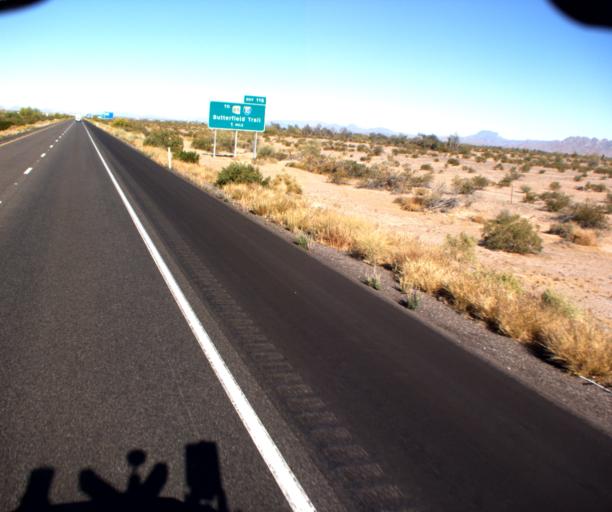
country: US
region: Arizona
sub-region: Maricopa County
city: Gila Bend
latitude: 32.9207
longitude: -112.6496
